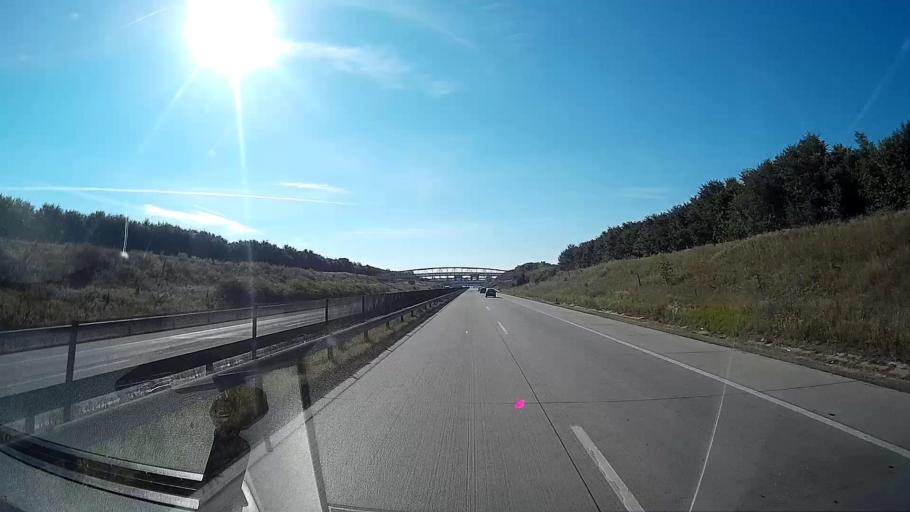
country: HU
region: Pest
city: Csomor
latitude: 47.5389
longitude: 19.2149
